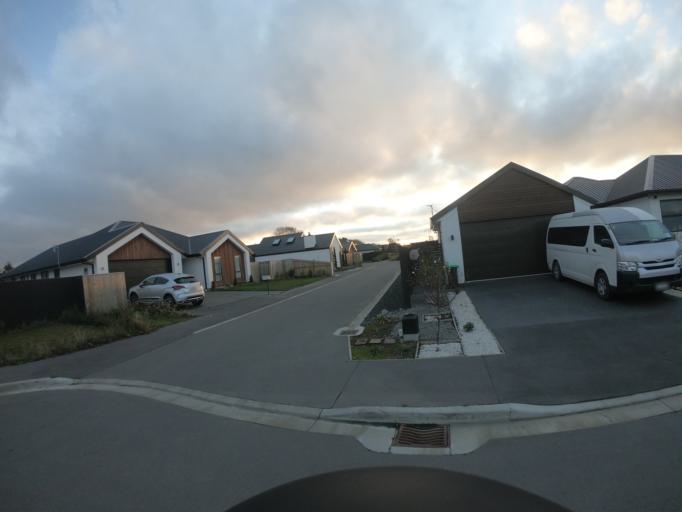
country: NZ
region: Canterbury
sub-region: Selwyn District
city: Prebbleton
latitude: -43.5663
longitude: 172.5592
